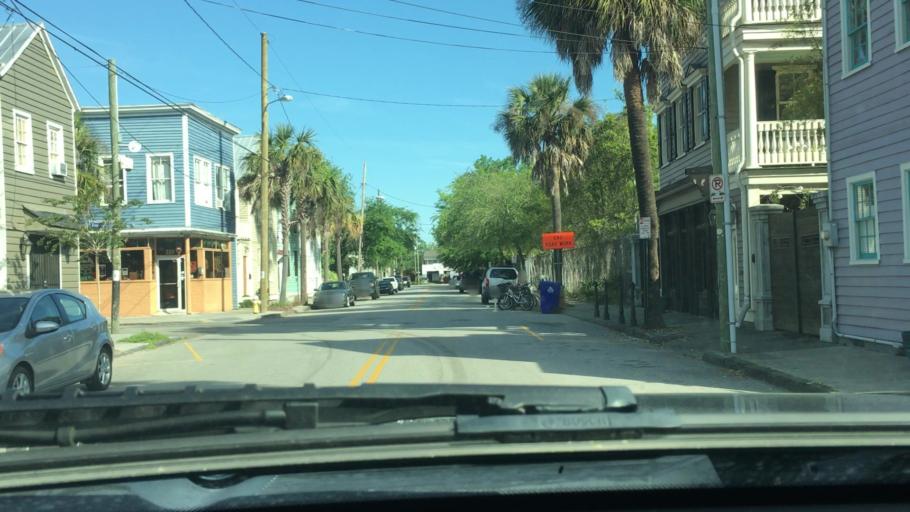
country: US
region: South Carolina
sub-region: Charleston County
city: Charleston
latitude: 32.7933
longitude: -79.9431
